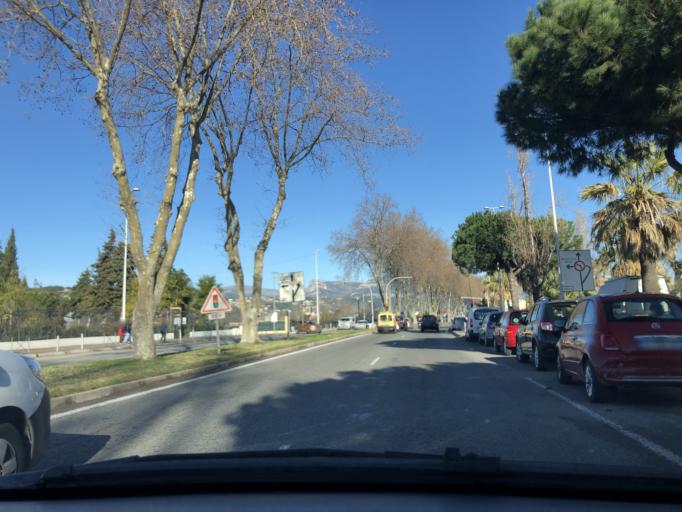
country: FR
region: Provence-Alpes-Cote d'Azur
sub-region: Departement des Alpes-Maritimes
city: Saint-Laurent-du-Var
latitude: 43.6804
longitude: 7.1996
